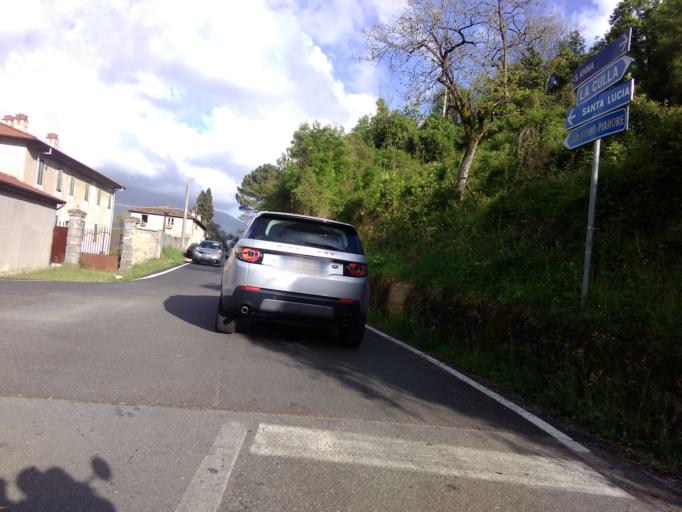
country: IT
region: Tuscany
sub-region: Provincia di Lucca
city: Piano di Mommio
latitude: 43.9500
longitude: 10.2725
